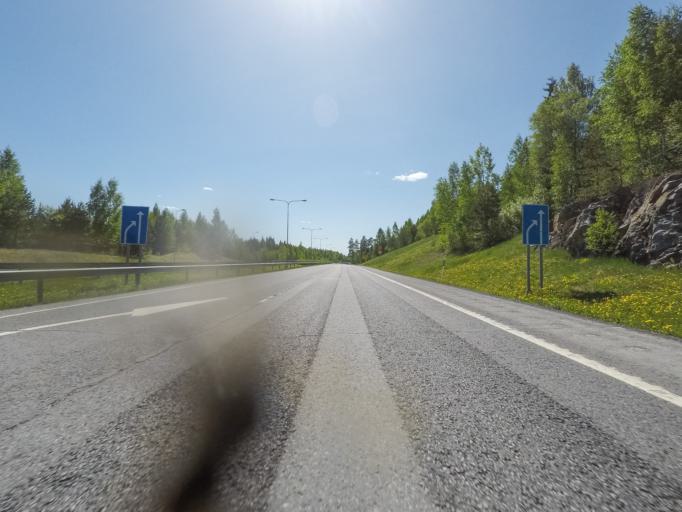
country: FI
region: Pirkanmaa
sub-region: Etelae-Pirkanmaa
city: Toijala
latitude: 61.1933
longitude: 23.8123
